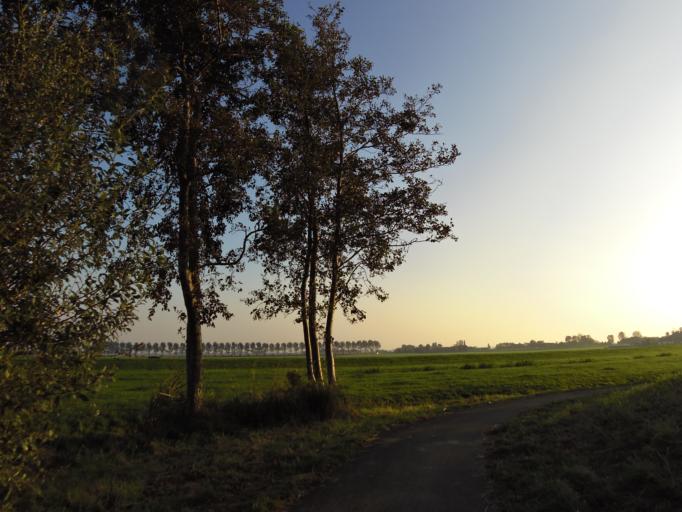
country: NL
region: South Holland
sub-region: Gemeente Kaag en Braassem
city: Oude Wetering
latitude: 52.1702
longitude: 4.6091
